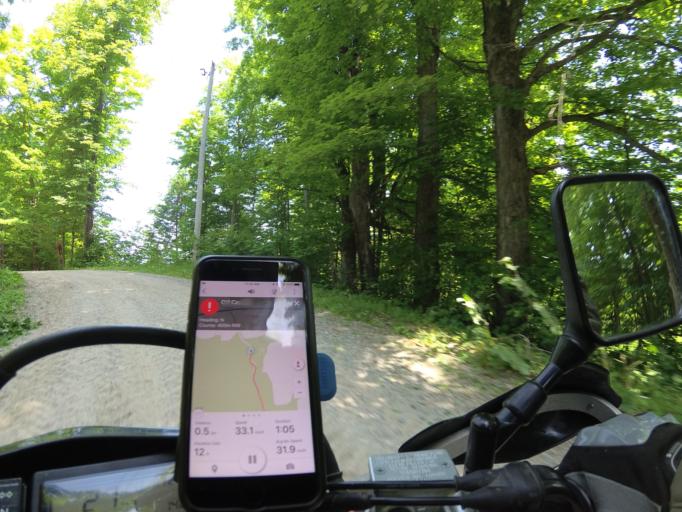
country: CA
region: Ontario
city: Skatepark
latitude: 44.7299
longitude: -76.8427
